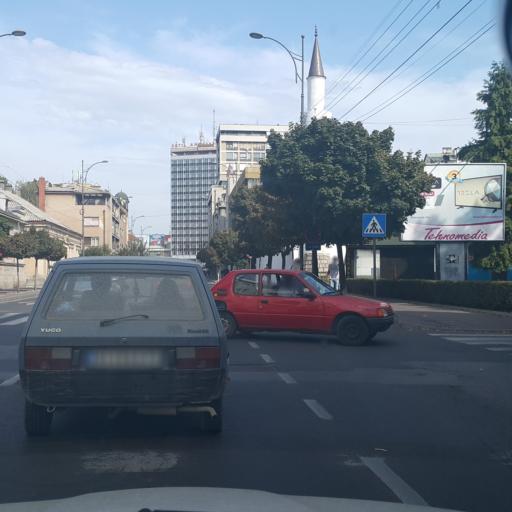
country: RS
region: Central Serbia
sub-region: Nisavski Okrug
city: Nis
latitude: 43.3204
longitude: 21.8925
